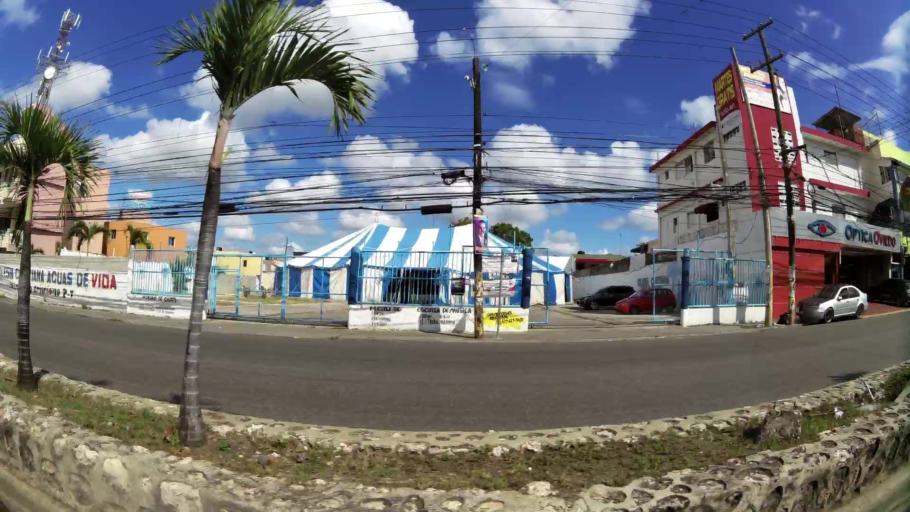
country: DO
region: Santo Domingo
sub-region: Santo Domingo
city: Santo Domingo Este
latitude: 18.5141
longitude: -69.8442
